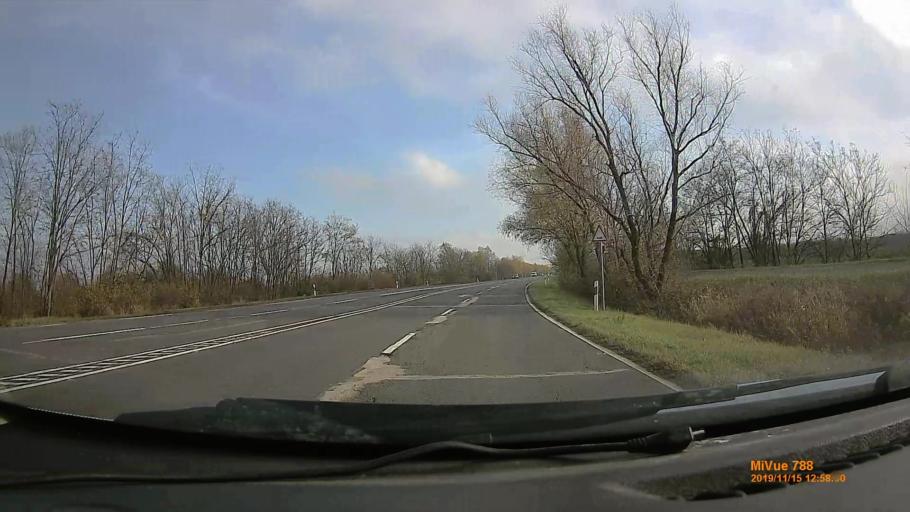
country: HU
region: Bekes
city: Bekescsaba
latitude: 46.6715
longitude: 21.1818
